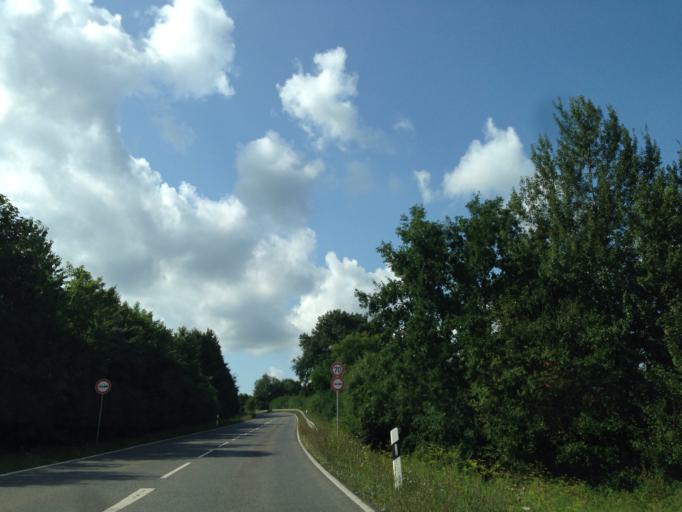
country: DE
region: Bavaria
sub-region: Upper Franconia
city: Burgebrach
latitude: 49.8235
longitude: 10.7372
